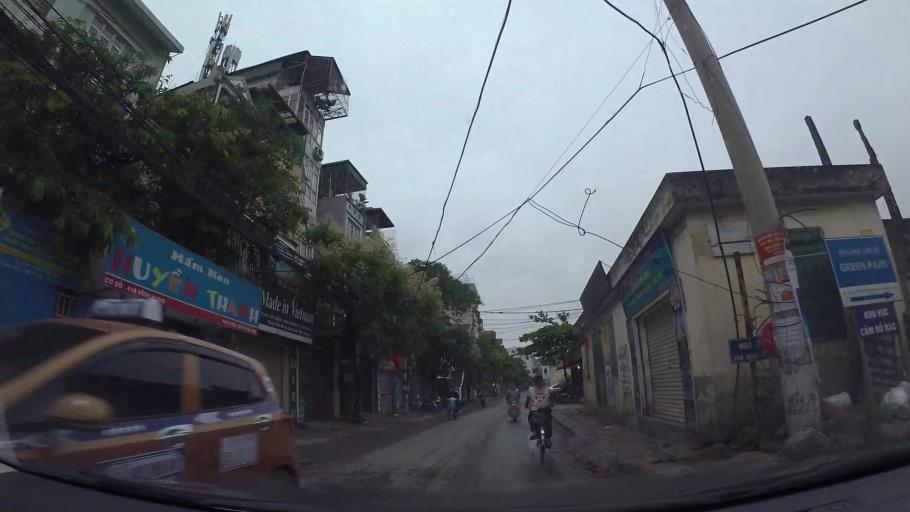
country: VN
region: Ha Noi
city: Hai BaTrung
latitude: 20.9959
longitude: 105.8796
